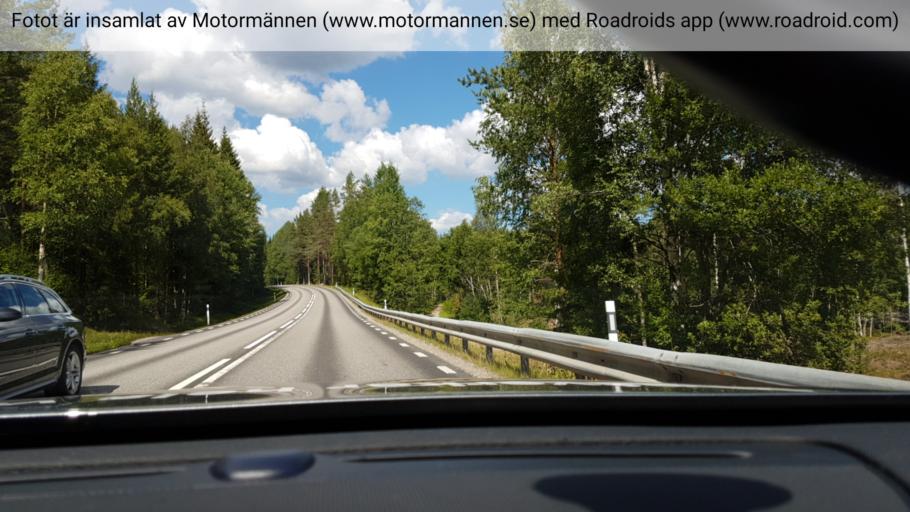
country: SE
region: Dalarna
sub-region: Faluns Kommun
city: Bjursas
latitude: 60.7383
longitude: 15.4307
